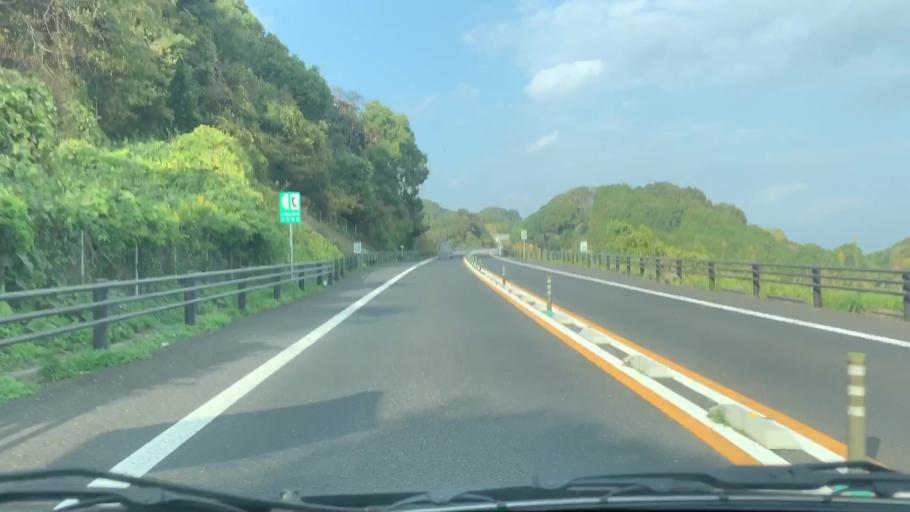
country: JP
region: Nagasaki
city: Sasebo
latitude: 33.0032
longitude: 129.7270
